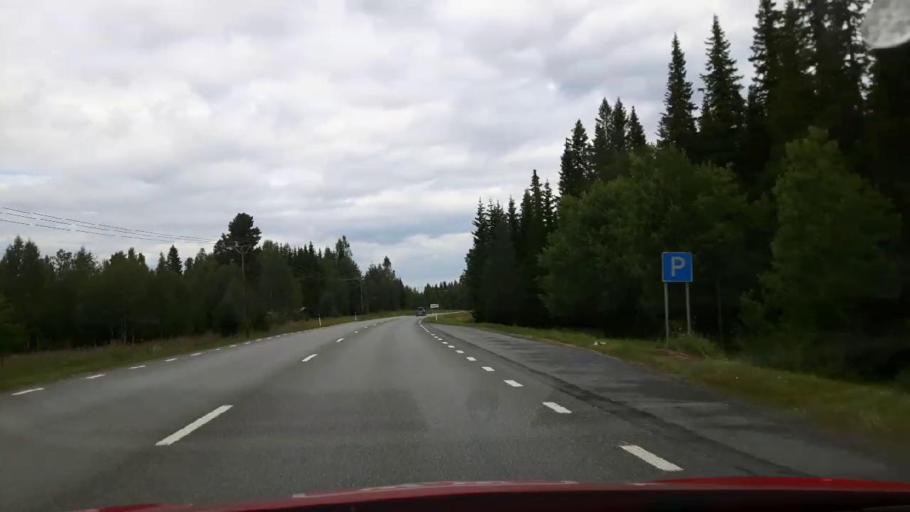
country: SE
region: Jaemtland
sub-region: Stroemsunds Kommun
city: Stroemsund
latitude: 63.6319
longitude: 15.3558
